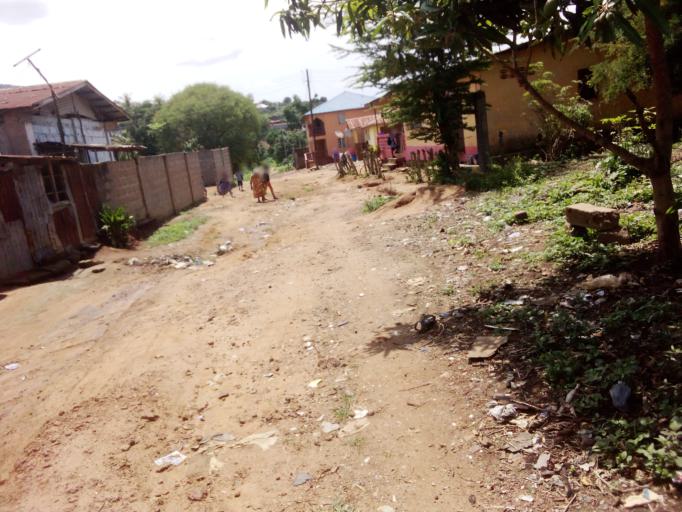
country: SL
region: Western Area
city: Waterloo
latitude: 8.3412
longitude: -13.0719
